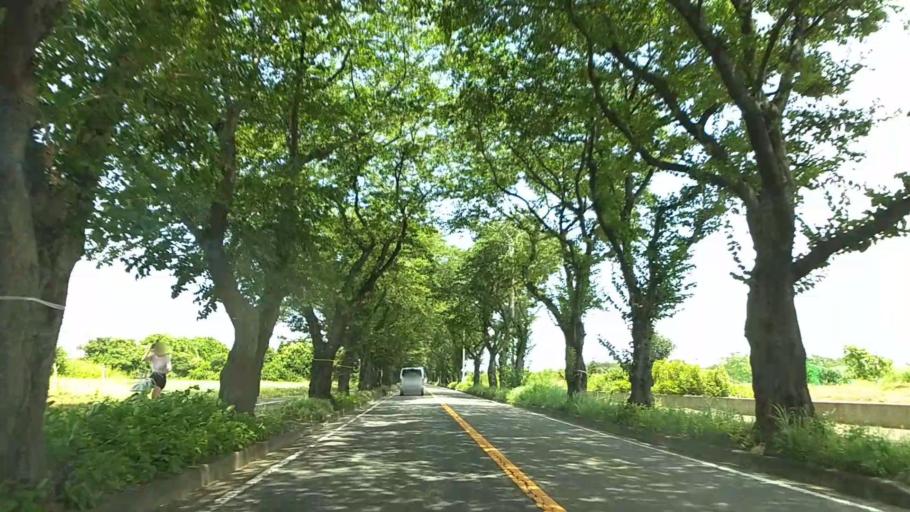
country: JP
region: Kanagawa
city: Minami-rinkan
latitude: 35.4911
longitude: 139.4802
